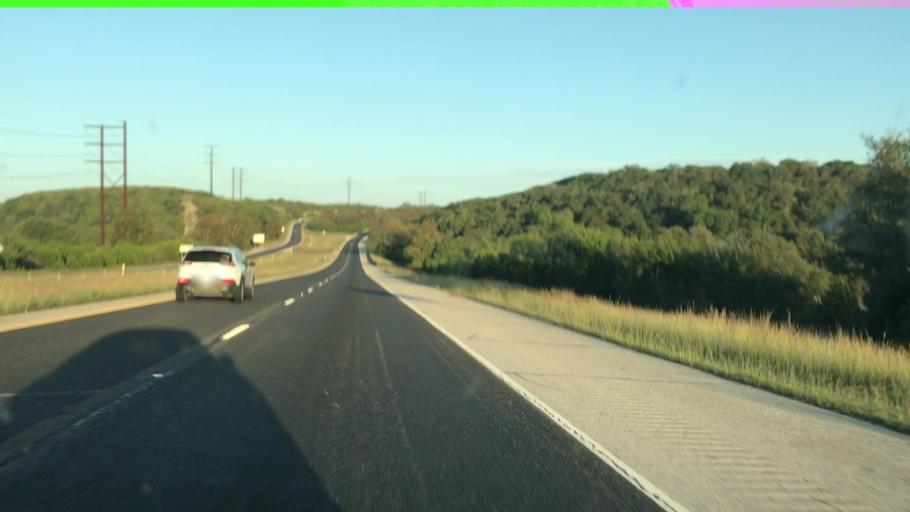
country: US
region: Texas
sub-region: Kerr County
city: Kerrville
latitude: 30.0694
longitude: -99.0905
